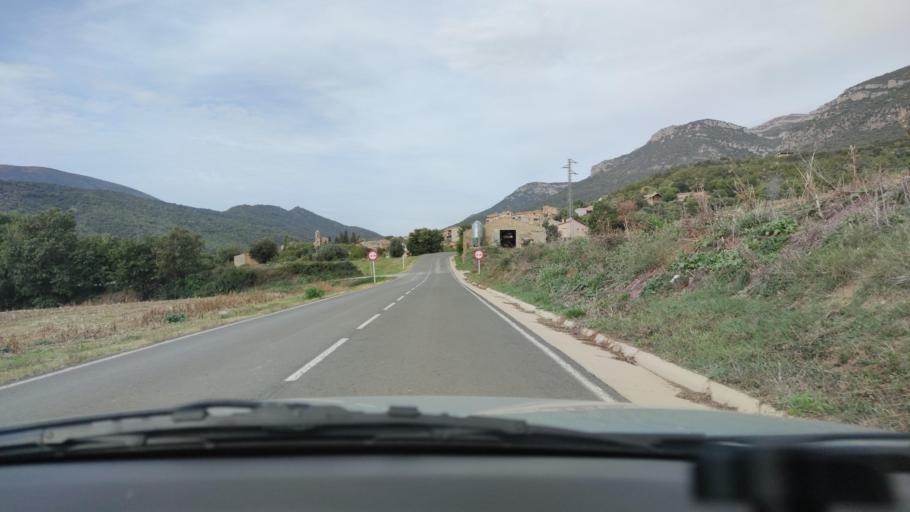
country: ES
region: Catalonia
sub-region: Provincia de Lleida
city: Artesa de Segre
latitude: 41.9918
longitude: 0.9993
